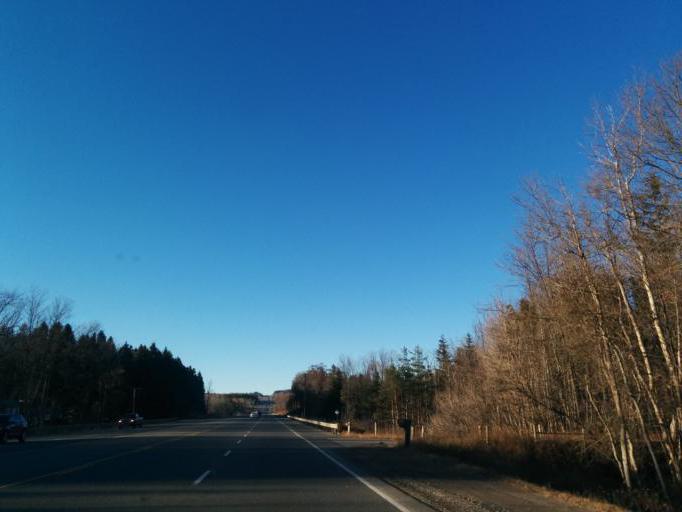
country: CA
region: Ontario
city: Orangeville
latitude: 43.8246
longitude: -79.9475
